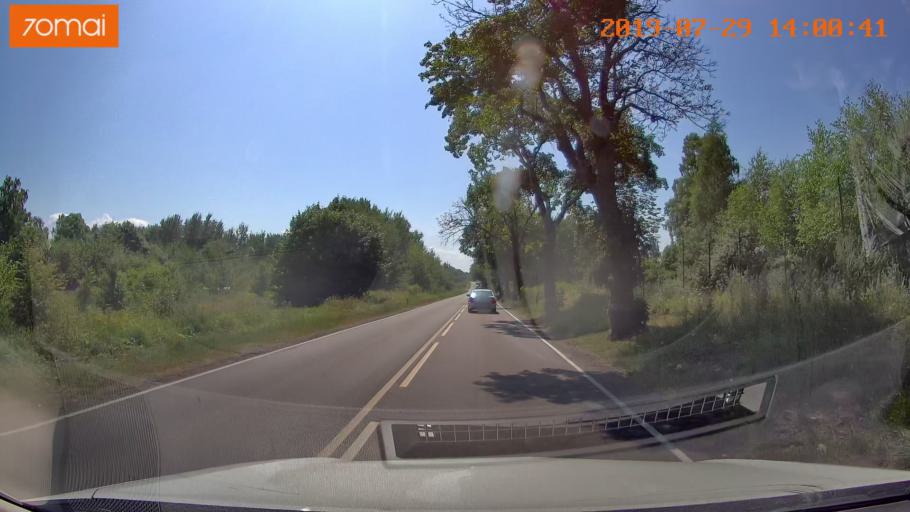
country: RU
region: Kaliningrad
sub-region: Gorod Kaliningrad
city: Baltiysk
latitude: 54.6764
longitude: 19.9265
